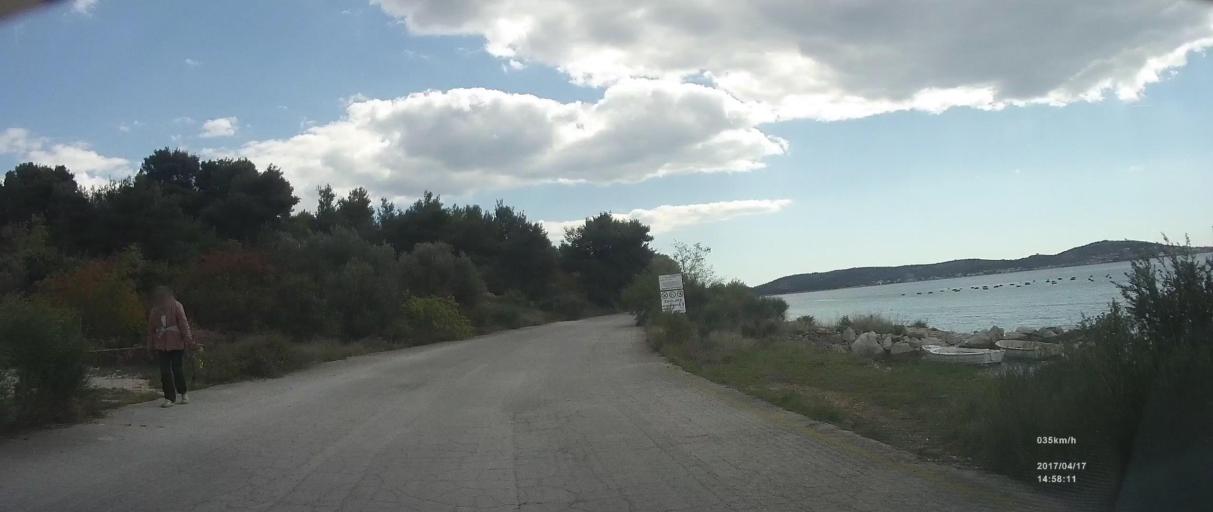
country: HR
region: Sibensko-Kniniska
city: Murter
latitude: 43.8402
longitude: 15.6280
